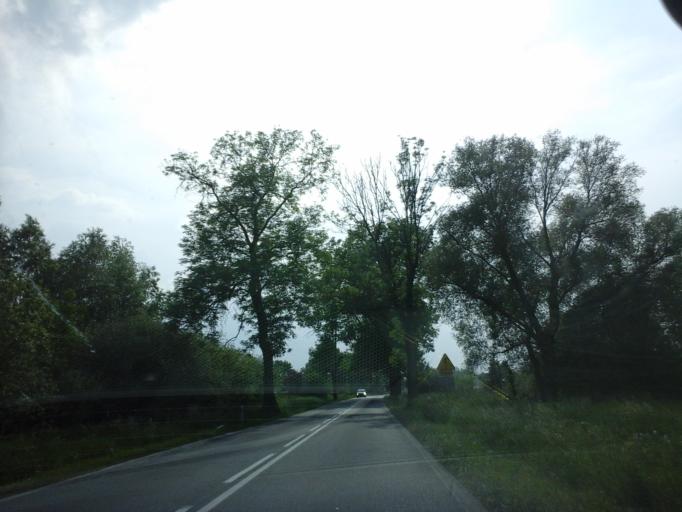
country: PL
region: West Pomeranian Voivodeship
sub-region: Powiat choszczenski
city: Choszczno
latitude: 53.1700
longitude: 15.4660
